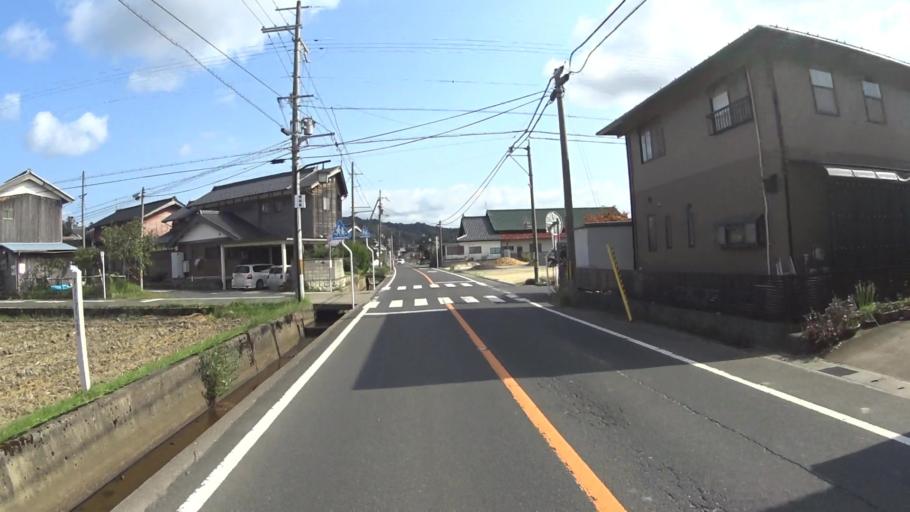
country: JP
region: Kyoto
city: Miyazu
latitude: 35.5921
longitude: 135.0990
